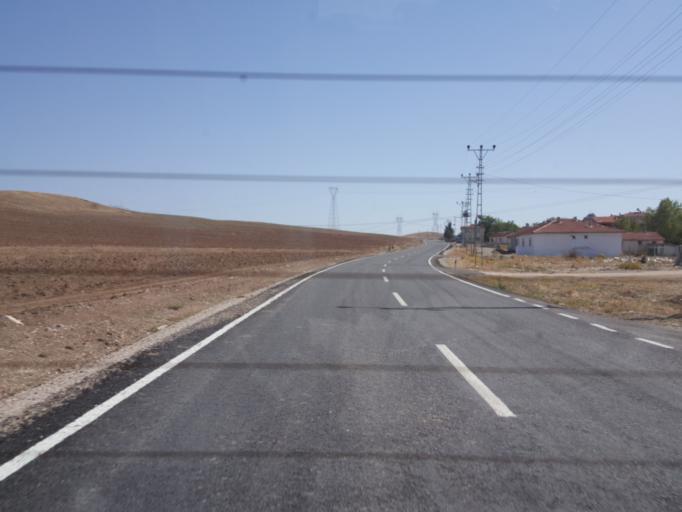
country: TR
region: Amasya
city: Dogantepe
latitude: 40.5912
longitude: 35.6138
